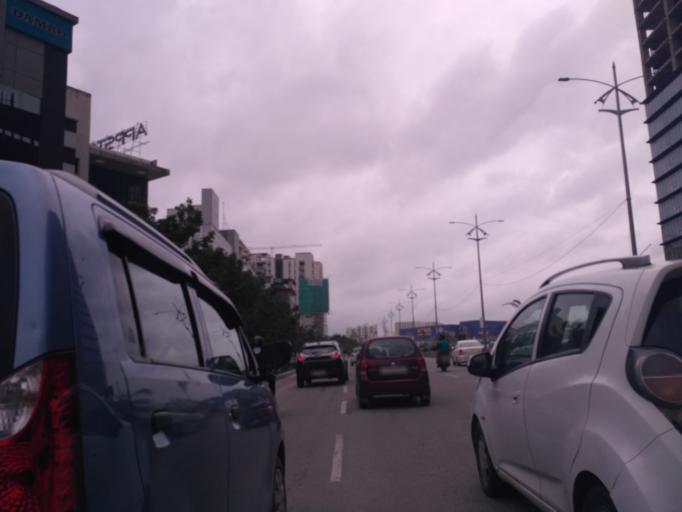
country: IN
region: Telangana
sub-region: Rangareddi
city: Kukatpalli
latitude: 17.4321
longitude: 78.3747
